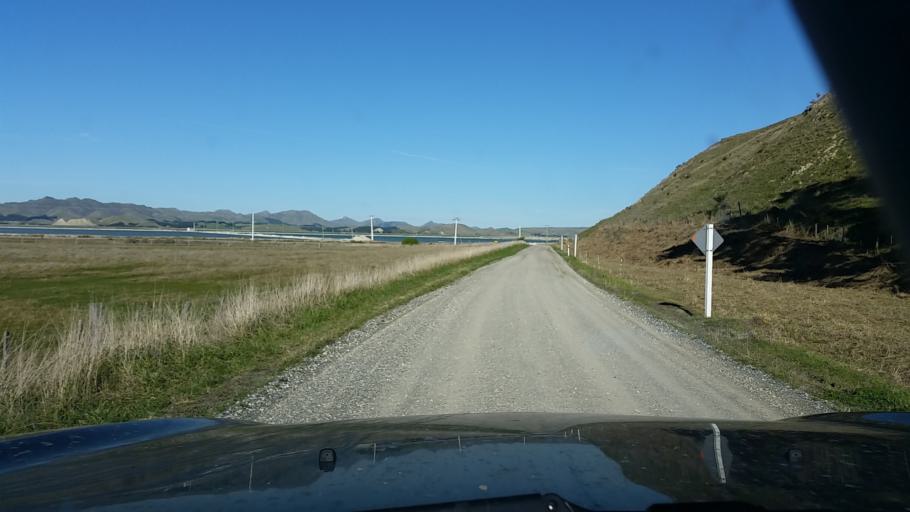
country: NZ
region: Marlborough
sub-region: Marlborough District
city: Blenheim
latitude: -41.7026
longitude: 174.1502
